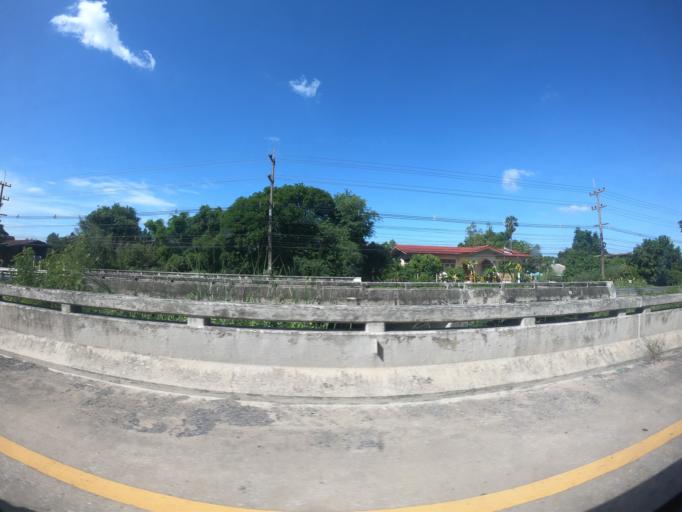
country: TH
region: Nakhon Nayok
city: Ban Na
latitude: 14.2519
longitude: 101.0966
